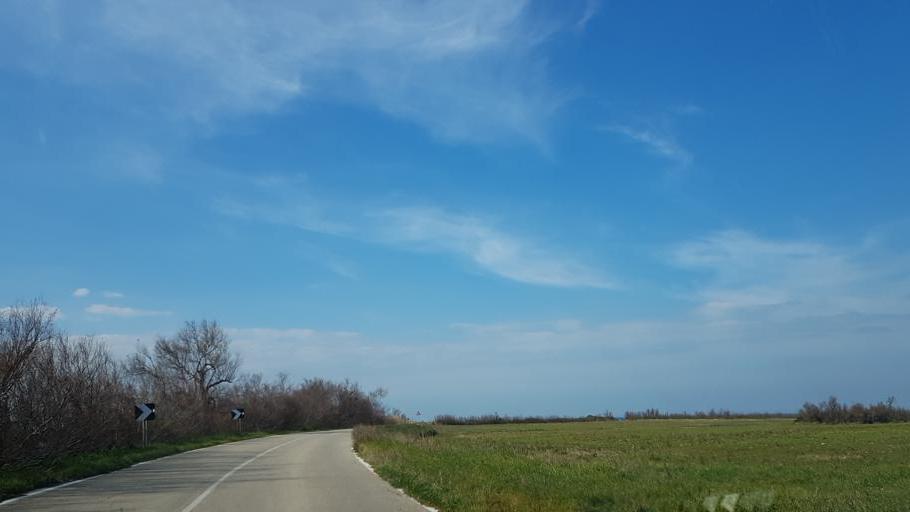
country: IT
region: Apulia
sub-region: Provincia di Brindisi
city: Brindisi
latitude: 40.6852
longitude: 17.8615
